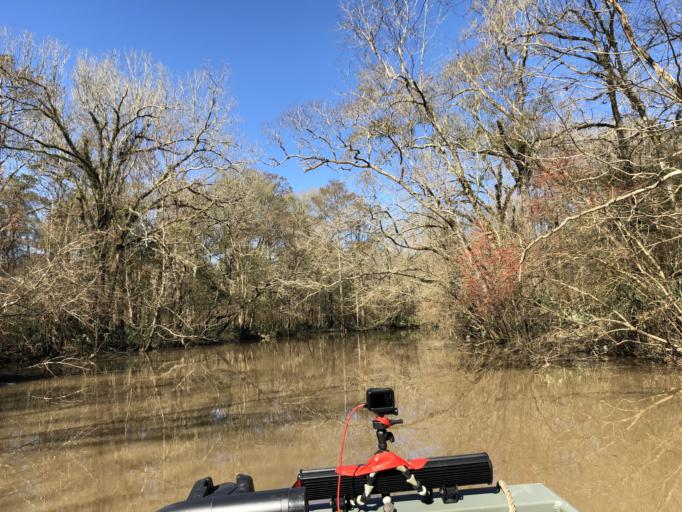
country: US
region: Louisiana
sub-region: Calcasieu Parish
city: Iowa
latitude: 30.3119
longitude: -93.0747
